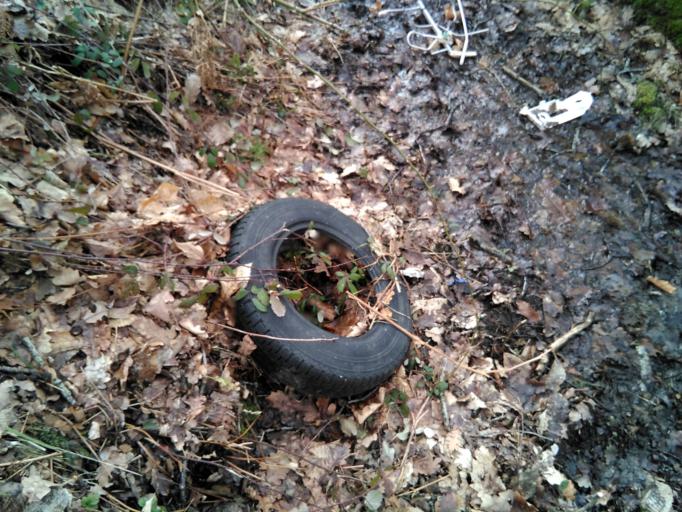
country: ES
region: Castille and Leon
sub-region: Provincia de Burgos
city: Espinosa de los Monteros
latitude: 43.0725
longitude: -3.5862
